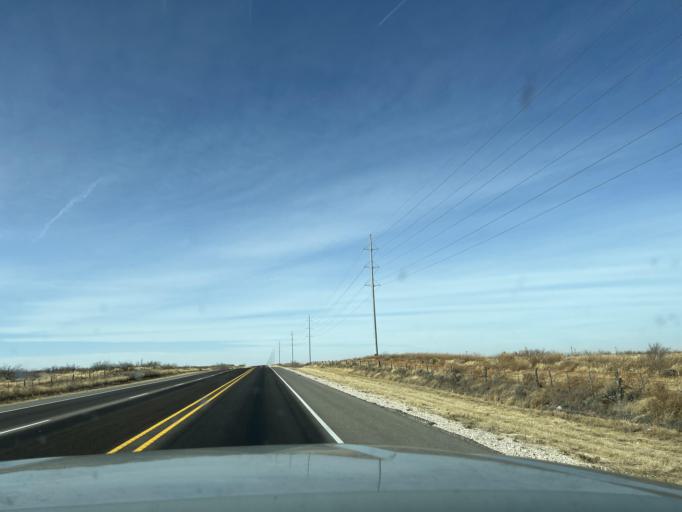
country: US
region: Texas
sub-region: Andrews County
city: Andrews
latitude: 32.3521
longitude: -102.7422
